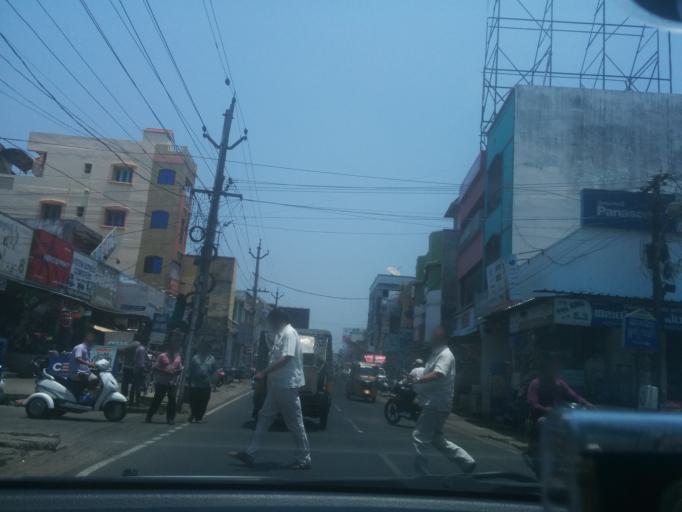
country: IN
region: Andhra Pradesh
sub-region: East Godavari
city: Rajahmundry
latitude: 16.9957
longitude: 81.7760
